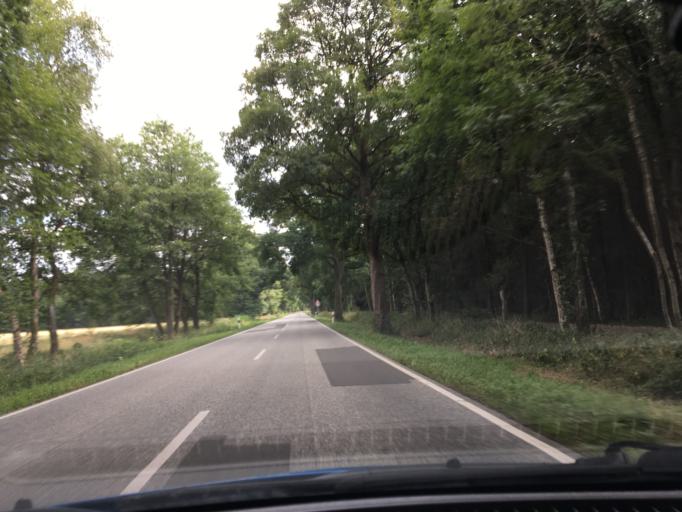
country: DE
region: Mecklenburg-Vorpommern
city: Lubtheen
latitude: 53.3586
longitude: 11.0848
